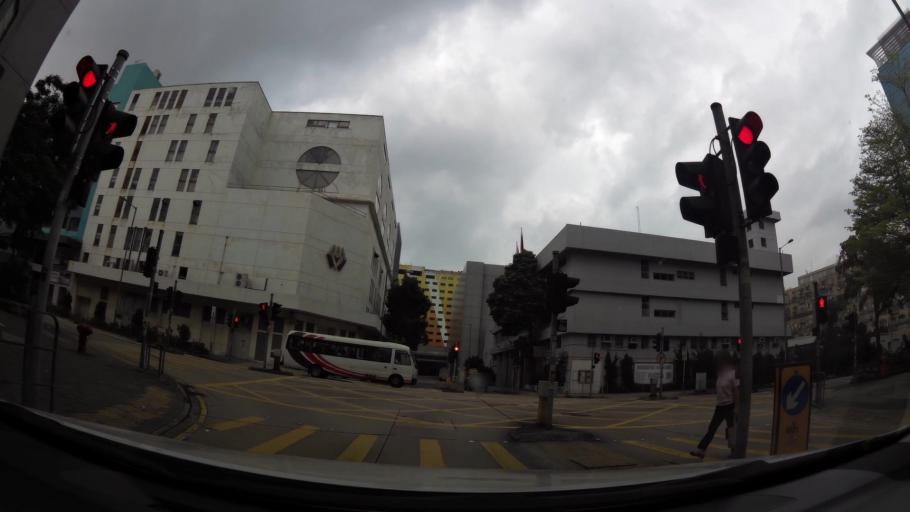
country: HK
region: Kowloon City
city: Kowloon
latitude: 22.3243
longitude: 114.2063
